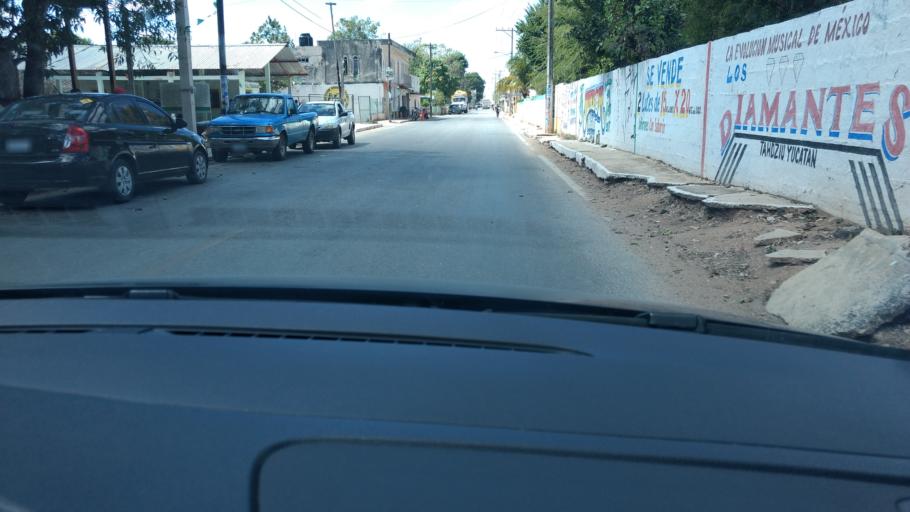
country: MX
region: Yucatan
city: Tzucacab
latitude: 20.0719
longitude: -89.0454
